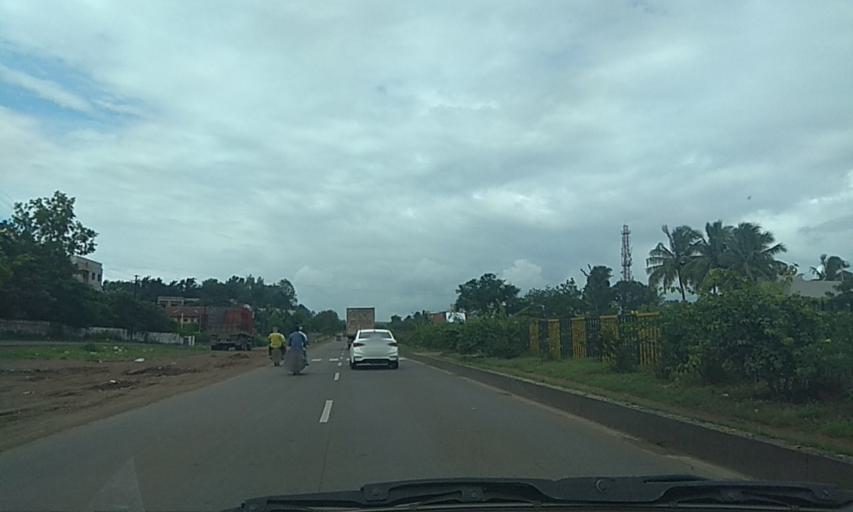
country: IN
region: Maharashtra
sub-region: Kolhapur
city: Kagal
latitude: 16.5850
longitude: 74.3095
